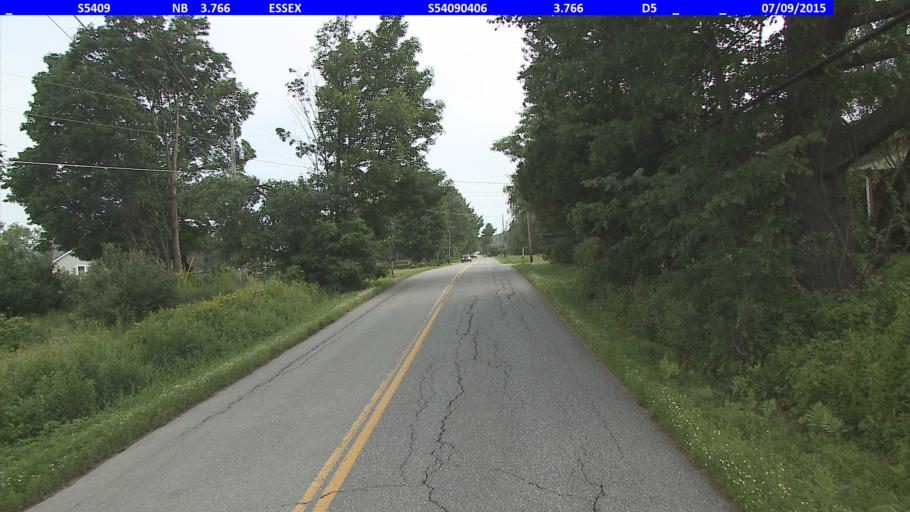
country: US
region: Vermont
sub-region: Chittenden County
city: Essex Junction
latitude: 44.5616
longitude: -73.0637
